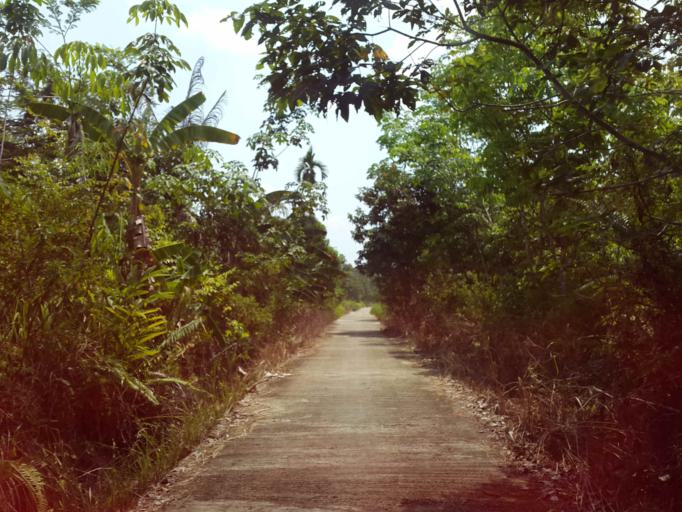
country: MY
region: Sarawak
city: Simanggang
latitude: 1.0351
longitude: 112.2251
